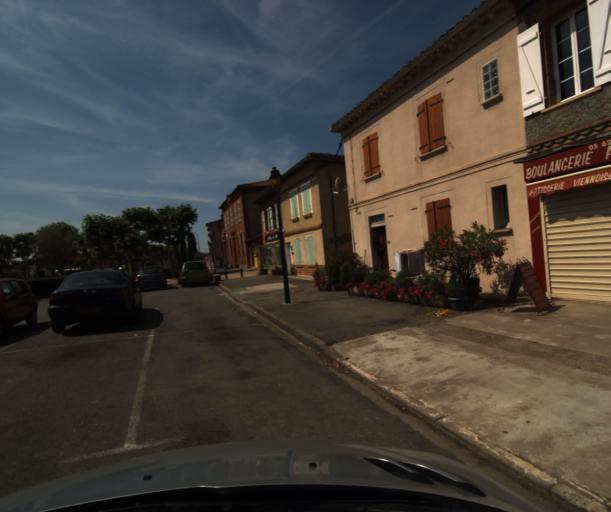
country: FR
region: Midi-Pyrenees
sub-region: Departement de la Haute-Garonne
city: Labastidette
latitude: 43.4666
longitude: 1.2161
